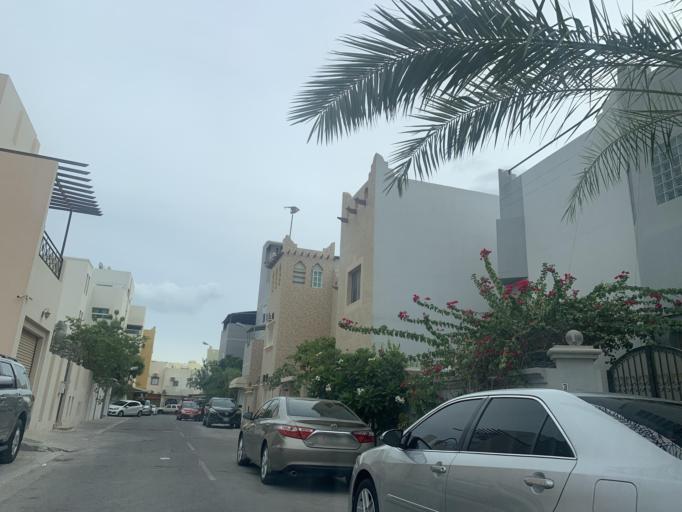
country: BH
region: Muharraq
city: Al Hadd
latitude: 26.2754
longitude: 50.6504
